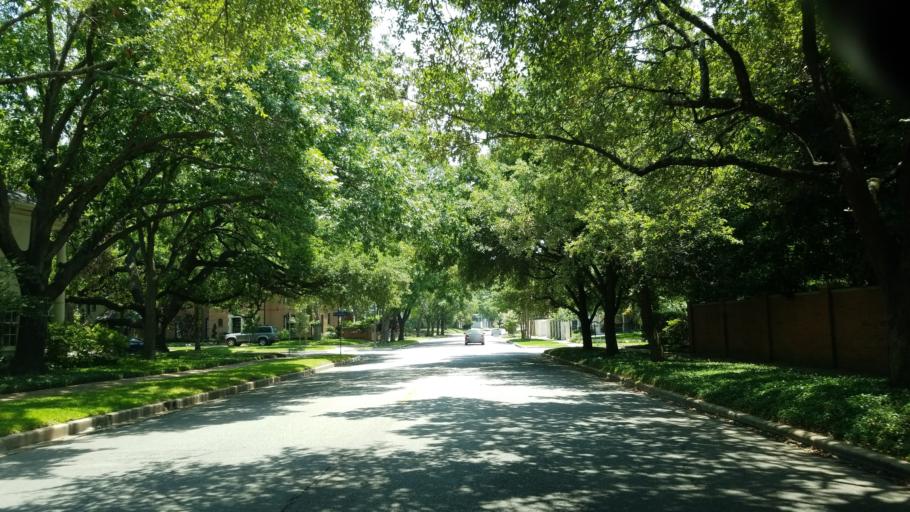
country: US
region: Texas
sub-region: Dallas County
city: Highland Park
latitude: 32.8316
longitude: -96.8100
